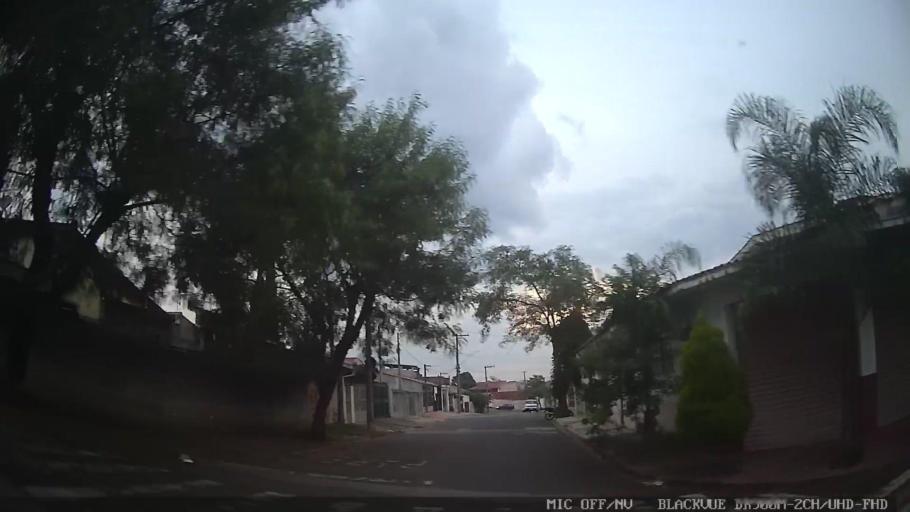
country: BR
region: Sao Paulo
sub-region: Atibaia
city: Atibaia
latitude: -23.1296
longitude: -46.5703
